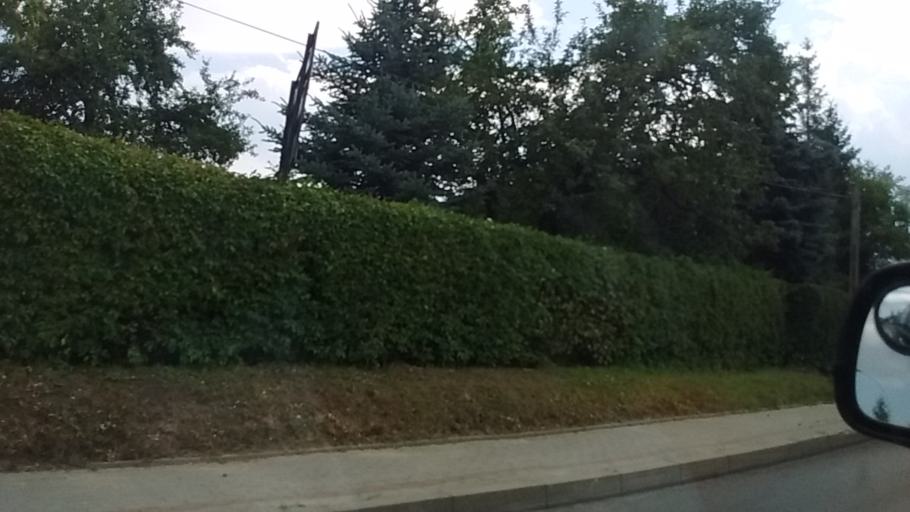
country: PL
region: Subcarpathian Voivodeship
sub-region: Powiat lezajski
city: Lezajsk
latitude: 50.2489
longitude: 22.4138
